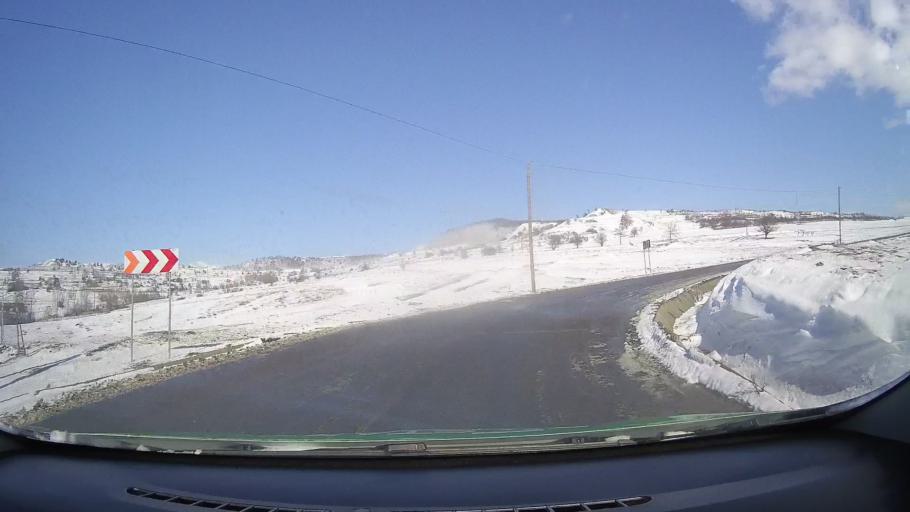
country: RO
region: Sibiu
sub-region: Comuna Avrig
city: Avrig
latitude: 45.7649
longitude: 24.3873
